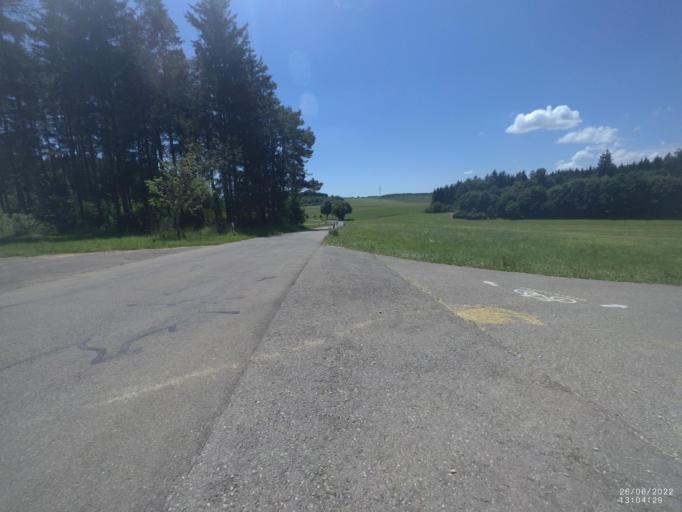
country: DE
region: Baden-Wuerttemberg
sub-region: Regierungsbezirk Stuttgart
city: Bohmenkirch
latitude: 48.6295
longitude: 9.9544
